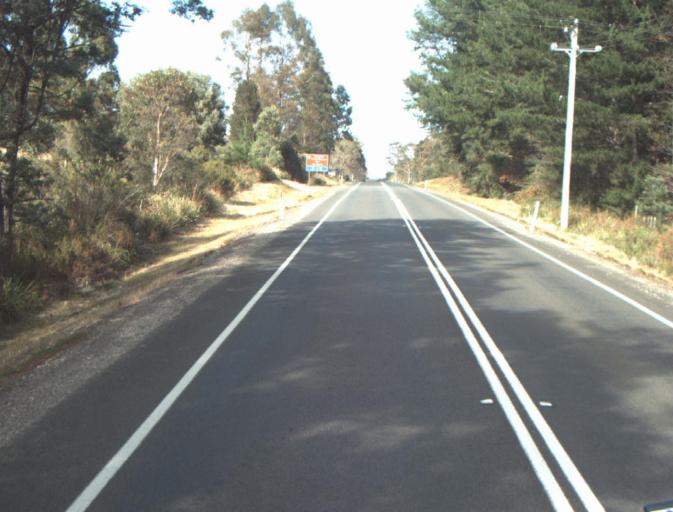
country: AU
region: Tasmania
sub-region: Launceston
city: Mayfield
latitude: -41.3098
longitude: 147.2019
